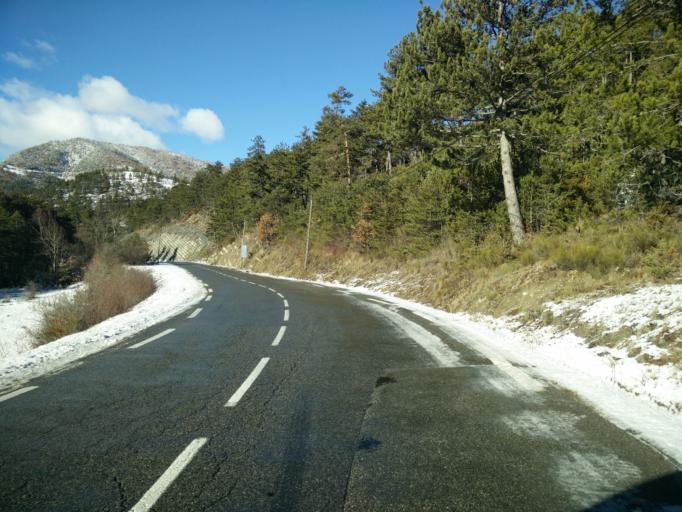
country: FR
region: Provence-Alpes-Cote d'Azur
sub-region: Departement des Alpes-de-Haute-Provence
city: Castellane
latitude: 43.9145
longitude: 6.5680
